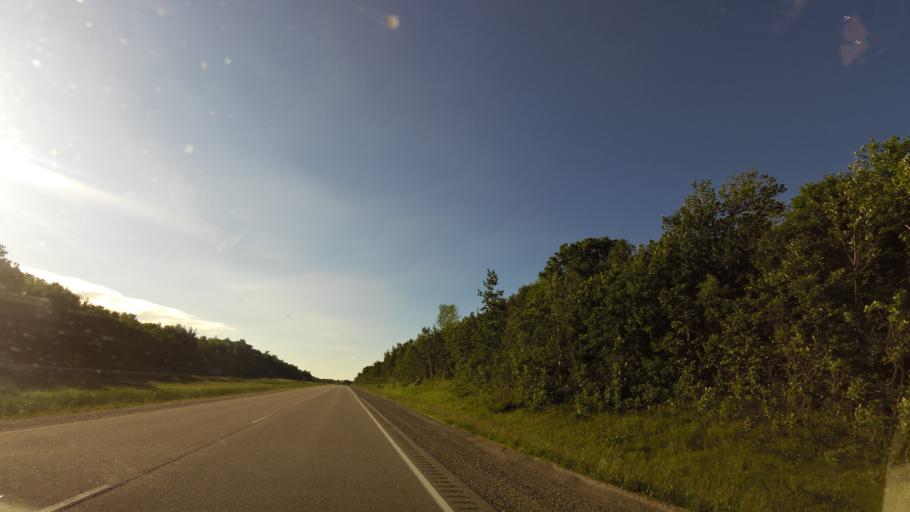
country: CA
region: Ontario
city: Midland
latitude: 44.7252
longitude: -79.6758
